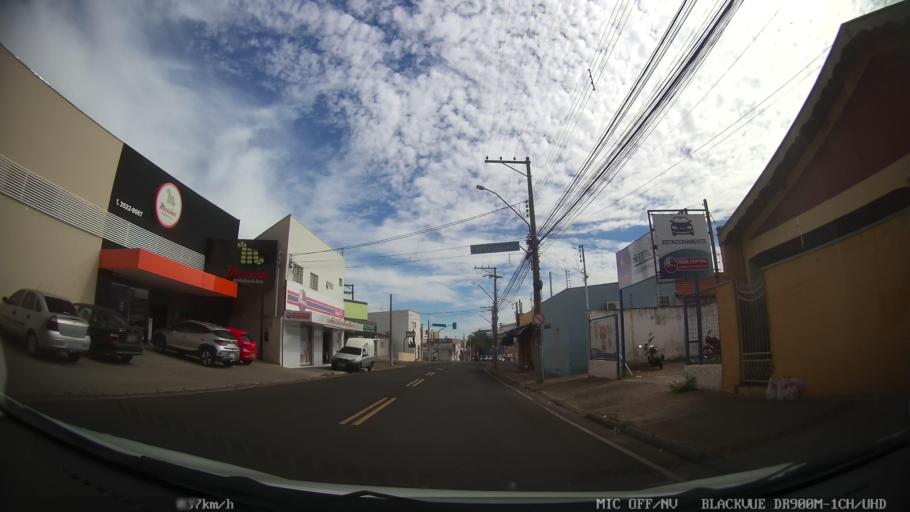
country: BR
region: Sao Paulo
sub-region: Catanduva
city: Catanduva
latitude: -21.1458
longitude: -48.9656
